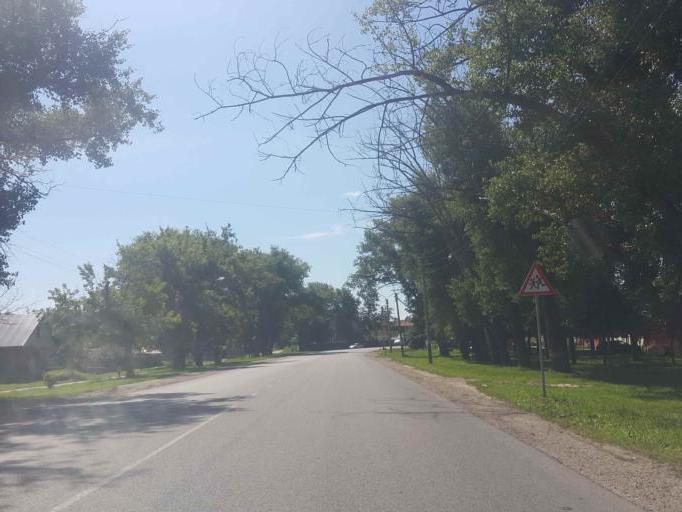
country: RU
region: Tambov
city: Pokrovo-Prigorodnoye
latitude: 52.7116
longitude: 41.4202
